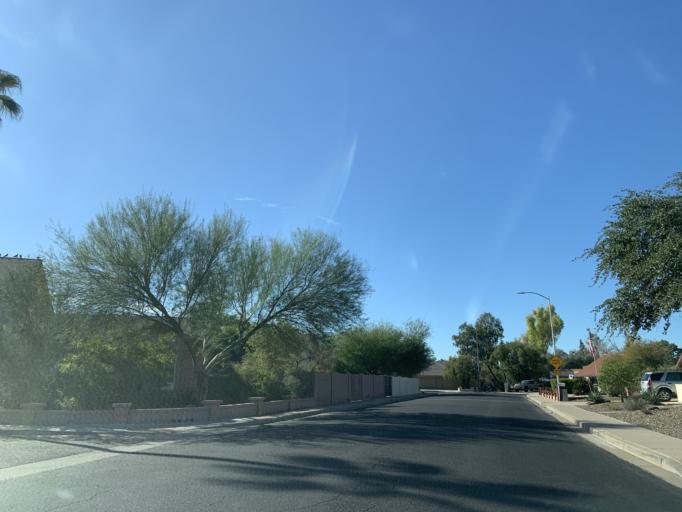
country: US
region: Arizona
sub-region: Maricopa County
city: San Carlos
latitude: 33.3703
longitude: -111.8665
